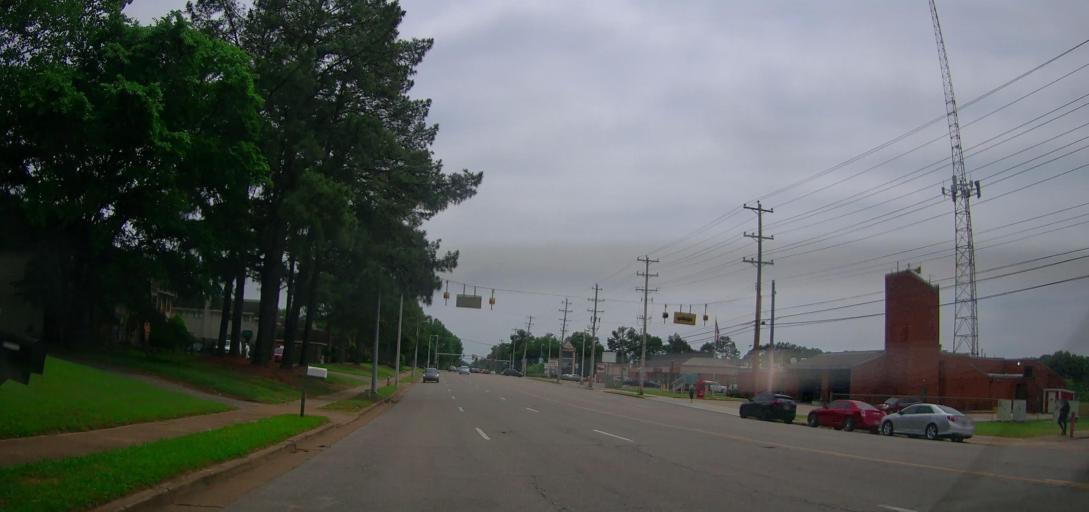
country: US
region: Tennessee
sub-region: Shelby County
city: Germantown
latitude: 35.0884
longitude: -89.8587
